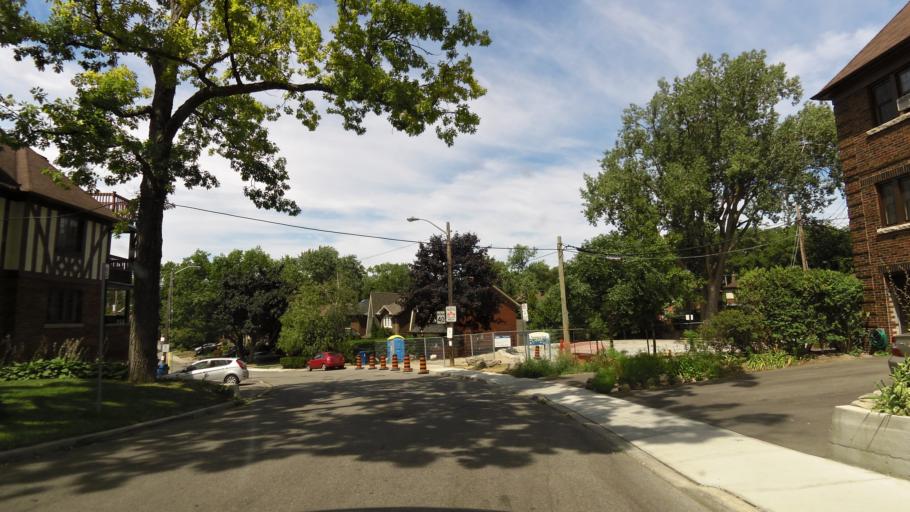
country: CA
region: Ontario
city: Etobicoke
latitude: 43.6479
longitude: -79.4887
